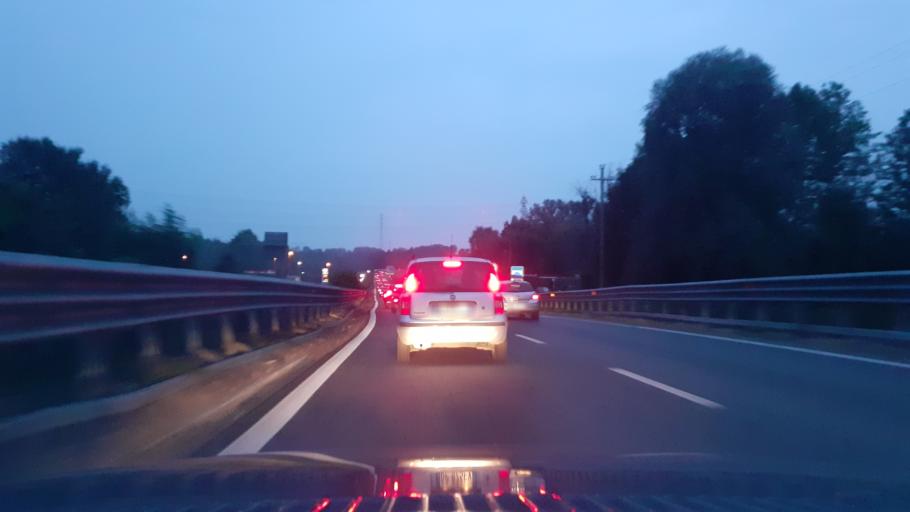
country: IT
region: Lombardy
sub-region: Provincia di Monza e Brianza
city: Capriano
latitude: 45.7359
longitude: 9.2495
